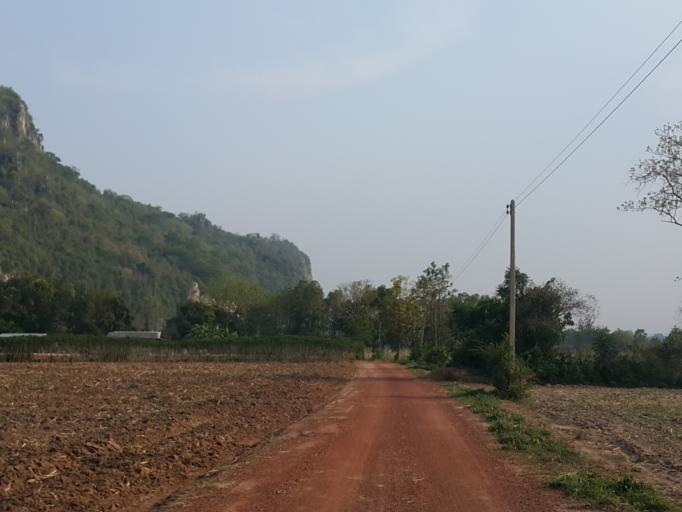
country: TH
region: Uthai Thani
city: Huai Khot
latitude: 15.3240
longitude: 99.6770
